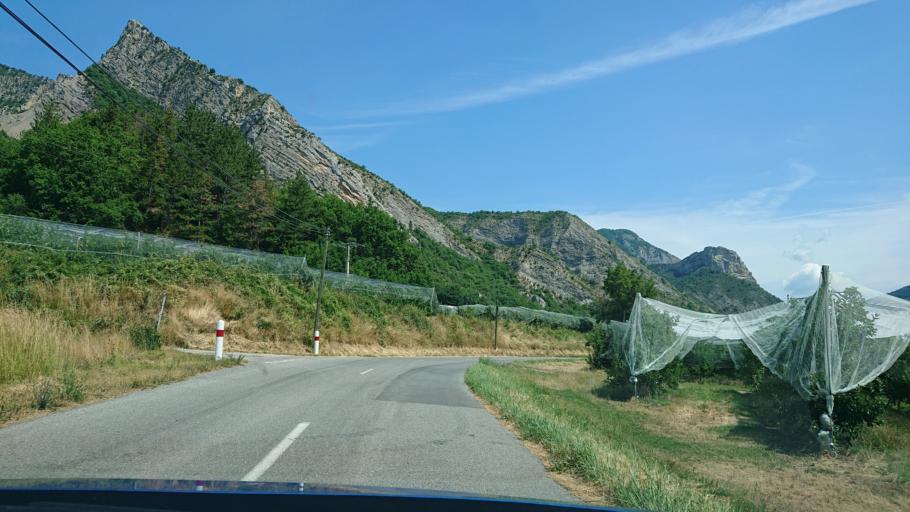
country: FR
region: Provence-Alpes-Cote d'Azur
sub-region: Departement des Hautes-Alpes
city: Tallard
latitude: 44.3616
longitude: 6.0503
